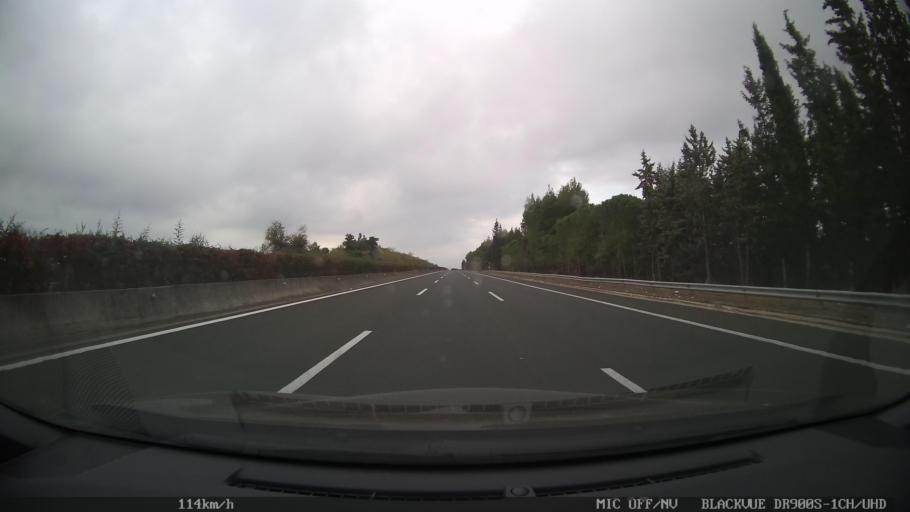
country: GR
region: Central Macedonia
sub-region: Nomos Pierias
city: Kitros
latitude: 40.3532
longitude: 22.5973
